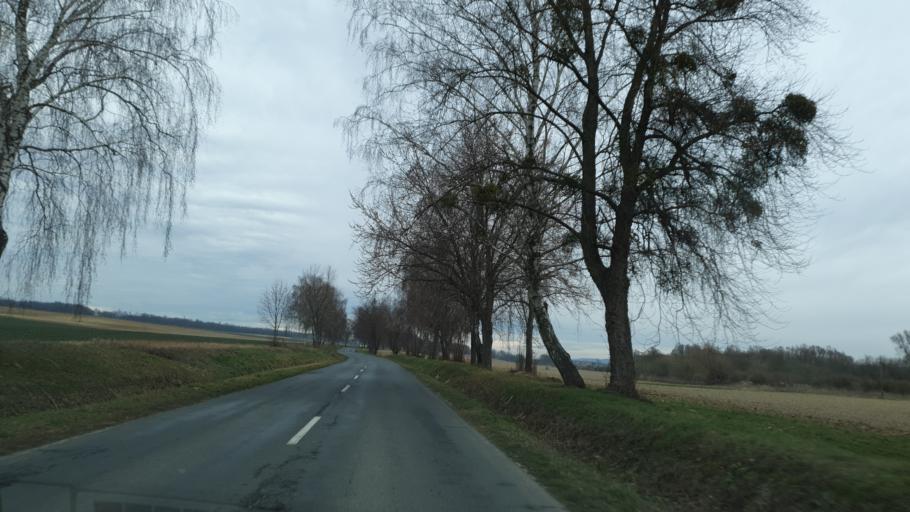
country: HU
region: Zala
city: Sarmellek
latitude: 46.7105
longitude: 17.1085
